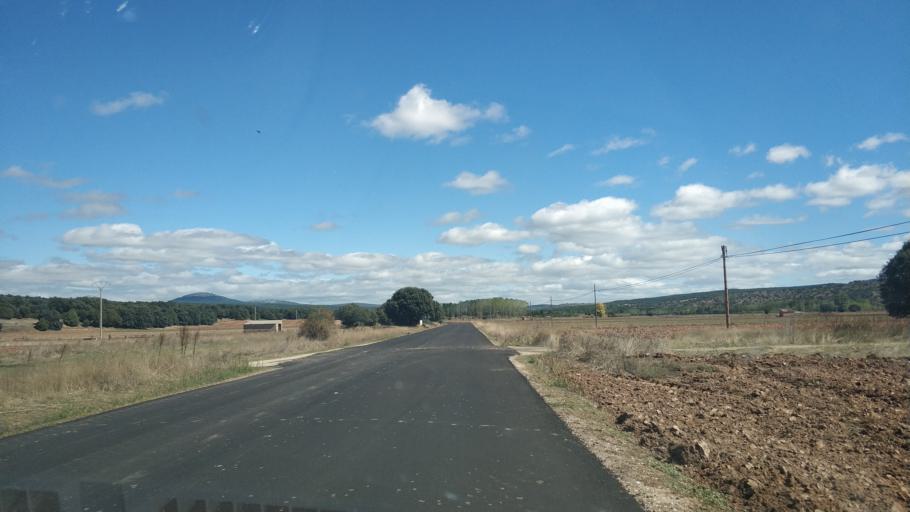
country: ES
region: Castille and Leon
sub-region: Provincia de Burgos
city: Puentedura
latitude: 42.0345
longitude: -3.6093
